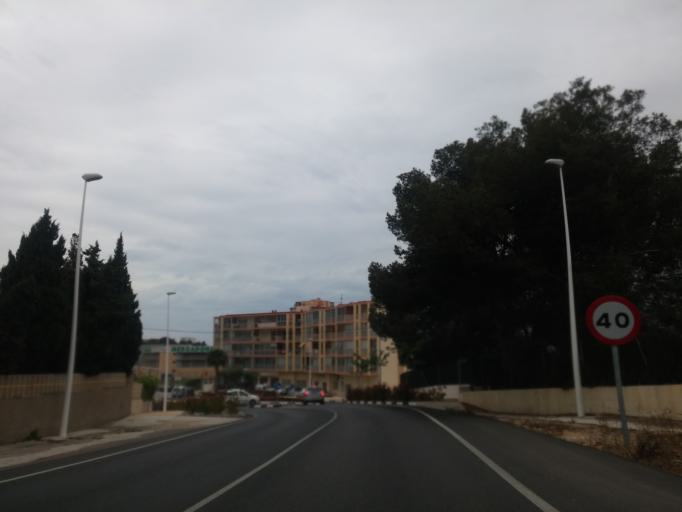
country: ES
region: Valencia
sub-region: Provincia de Alicante
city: Calp
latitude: 38.6523
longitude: 0.0734
